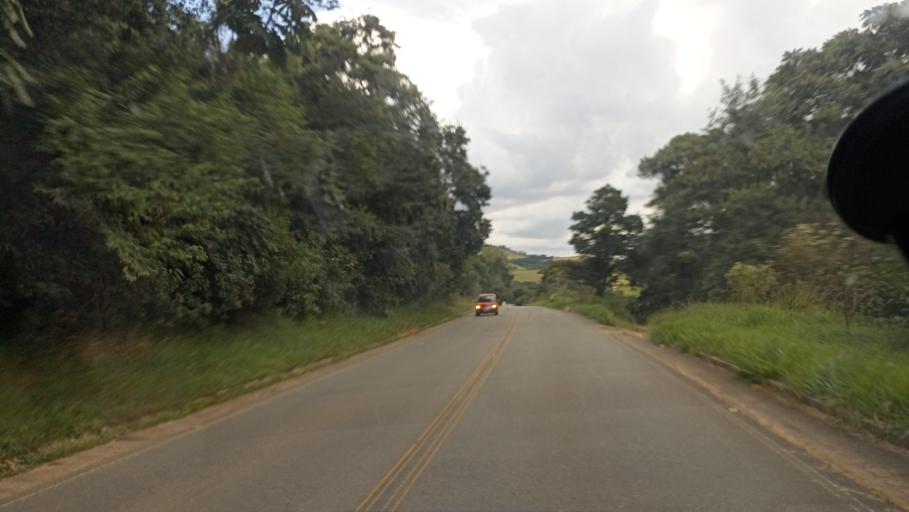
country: BR
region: Minas Gerais
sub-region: Cruzilia
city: Cruzilia
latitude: -21.8839
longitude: -44.8150
